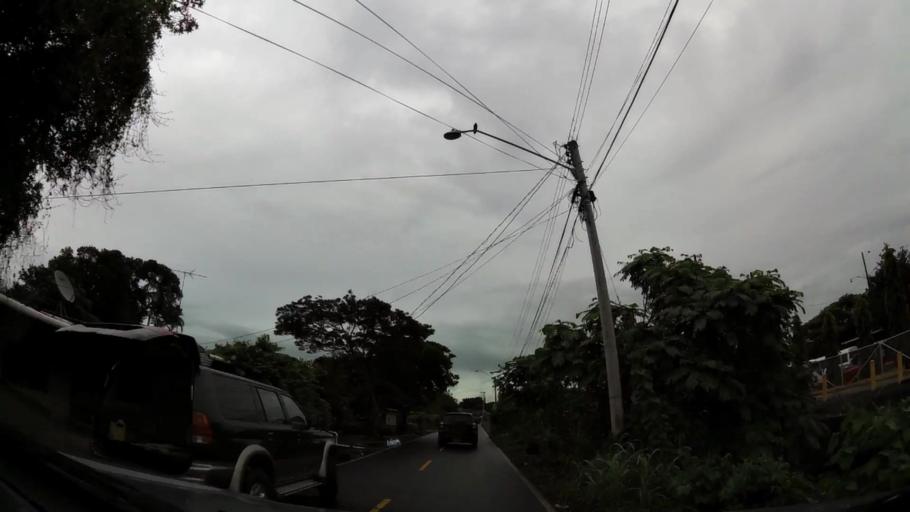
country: PA
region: Veraguas
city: Santiago de Veraguas
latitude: 8.1051
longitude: -80.9752
